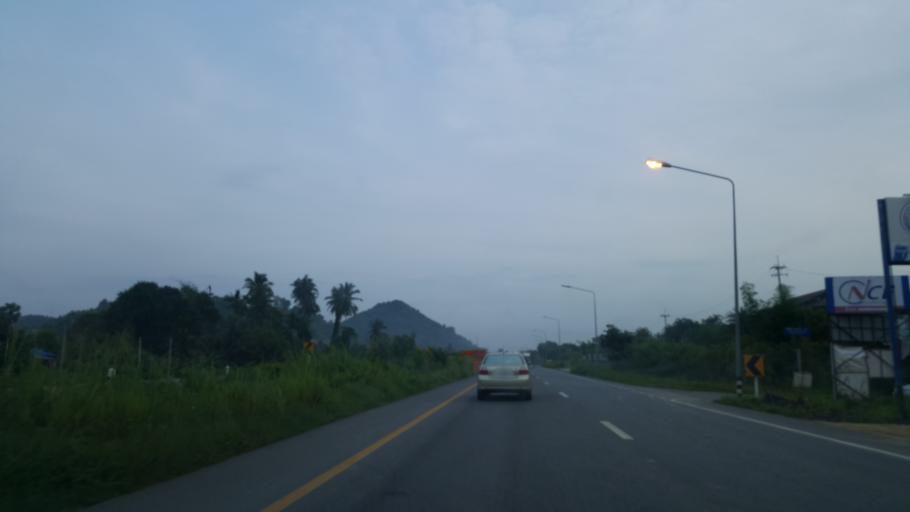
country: TH
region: Rayong
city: Ban Chang
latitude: 12.7412
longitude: 100.9906
